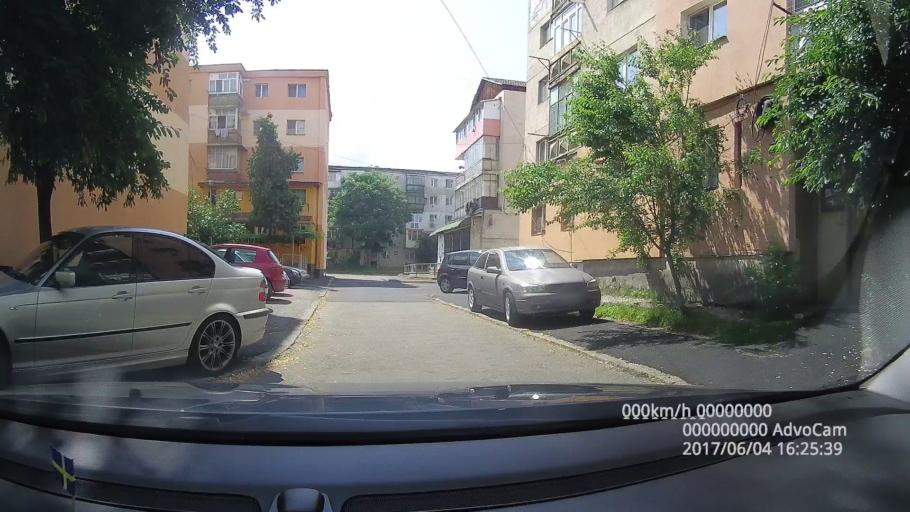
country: RO
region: Gorj
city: Targu Jiu
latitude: 45.0276
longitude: 23.2787
